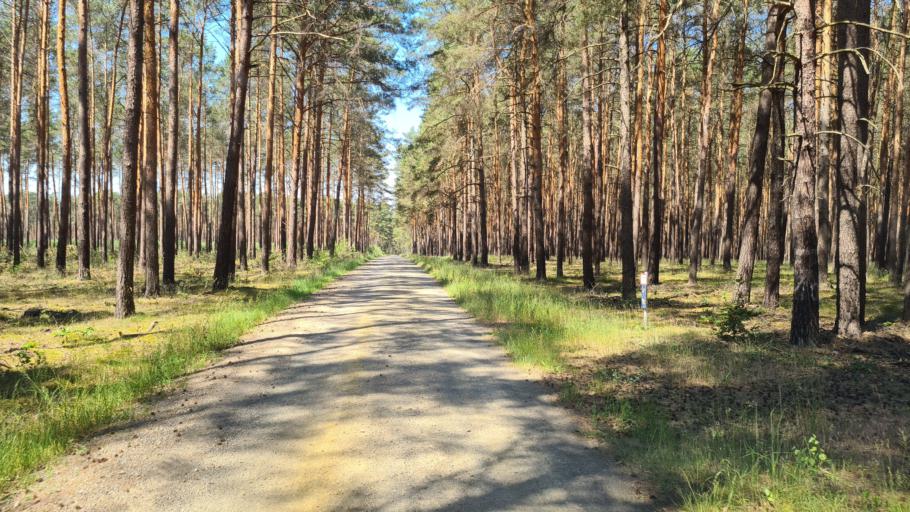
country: DE
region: Brandenburg
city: Schlieben
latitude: 51.7798
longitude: 13.3551
